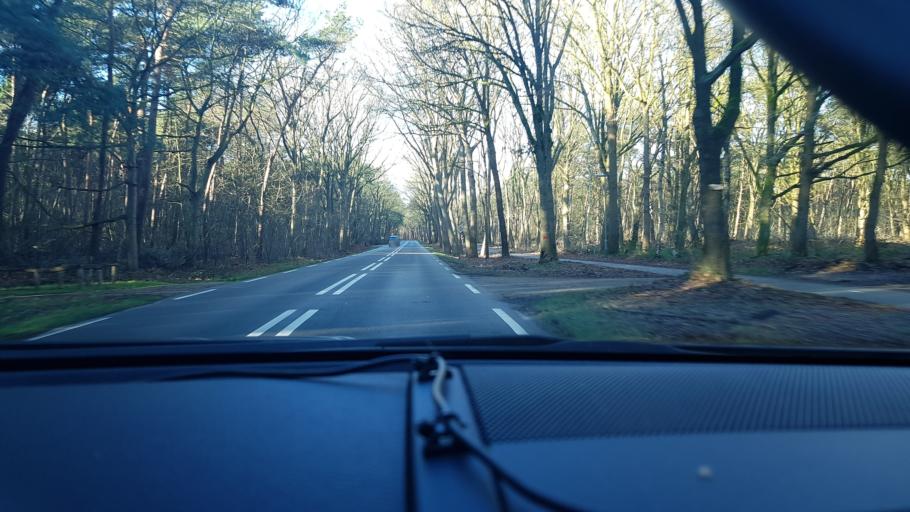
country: NL
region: Limburg
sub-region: Gemeente Beesel
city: Beesel
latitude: 51.3065
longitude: 6.0232
